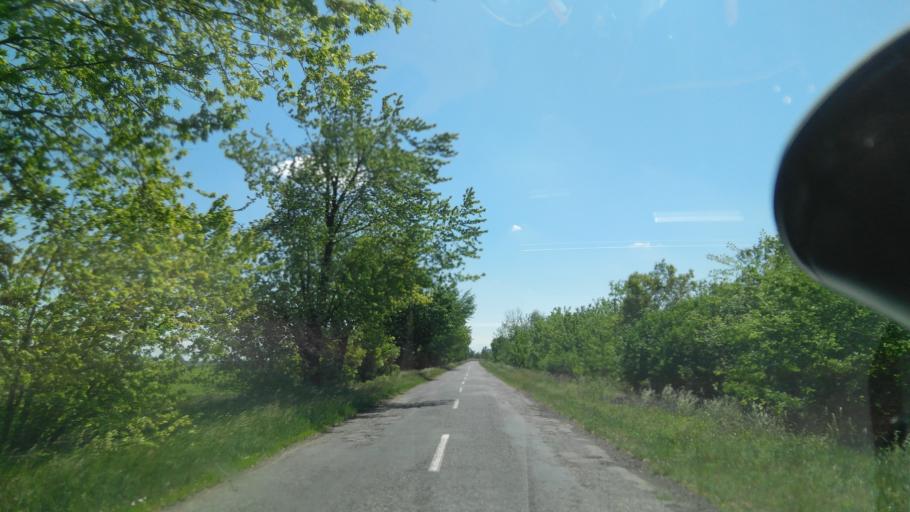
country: HU
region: Bekes
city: Kunagota
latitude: 46.4110
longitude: 21.0510
